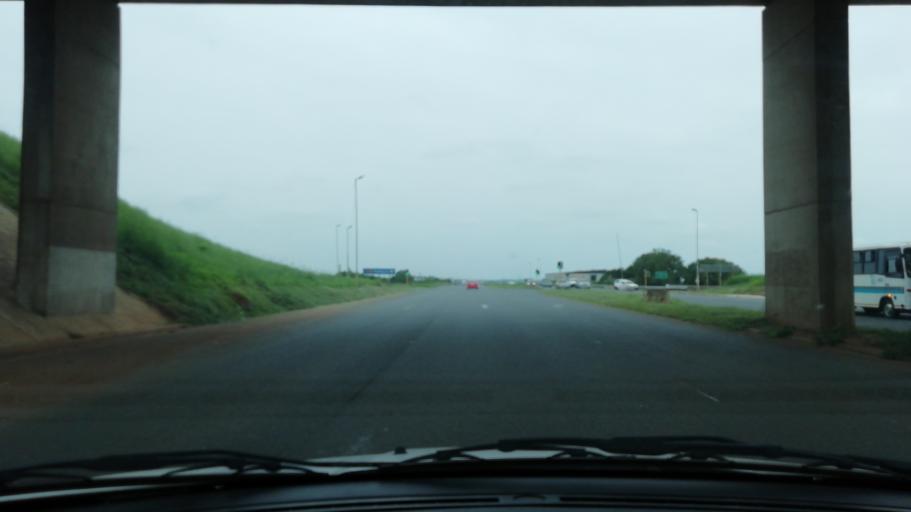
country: ZA
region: KwaZulu-Natal
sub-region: uThungulu District Municipality
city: Empangeni
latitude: -28.7688
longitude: 31.9306
